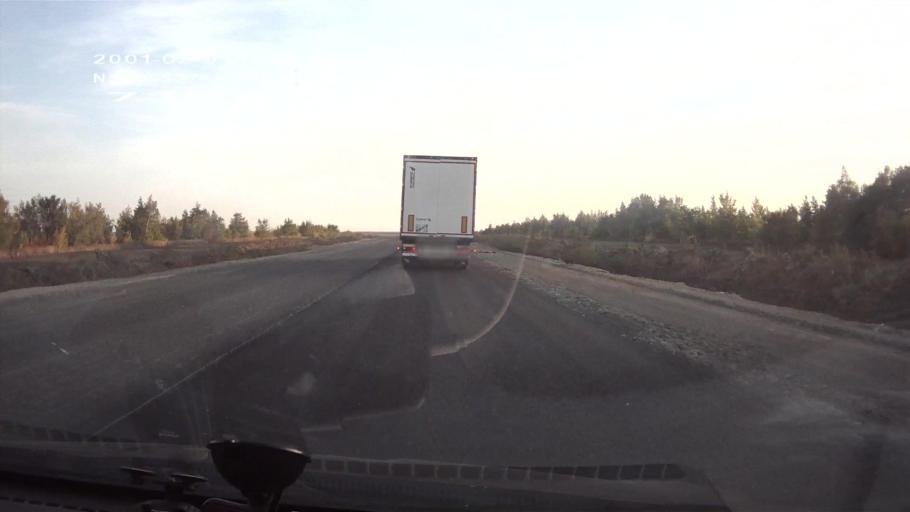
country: RU
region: Saratov
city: Krasnoarmeysk
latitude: 51.0024
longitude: 45.6147
